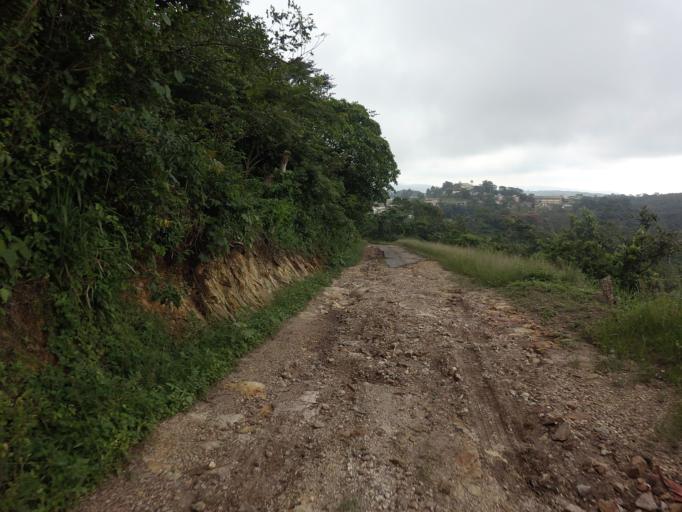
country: GH
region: Volta
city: Kpandu
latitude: 6.8406
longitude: 0.4323
